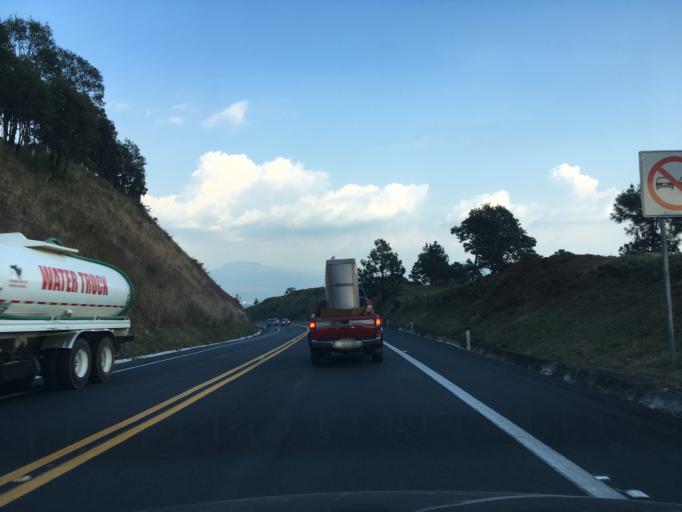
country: MX
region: Michoacan
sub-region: Uruapan
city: Toreo Bajo (El Toreo Bajo)
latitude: 19.4149
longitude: -101.9773
